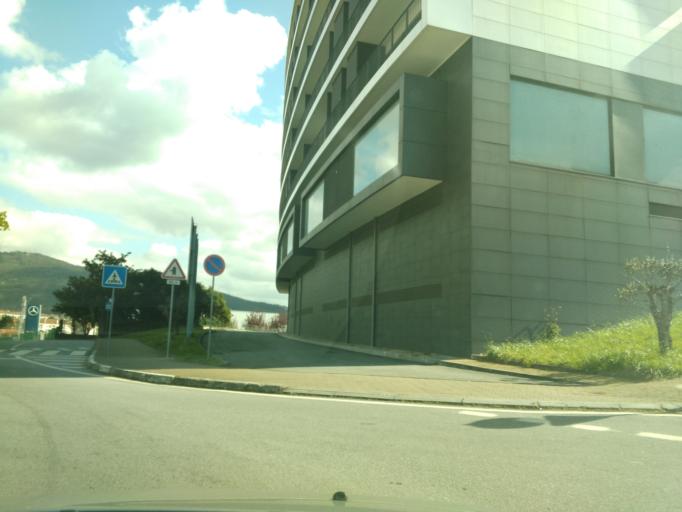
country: PT
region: Braga
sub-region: Braga
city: Braga
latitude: 41.5361
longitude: -8.4235
